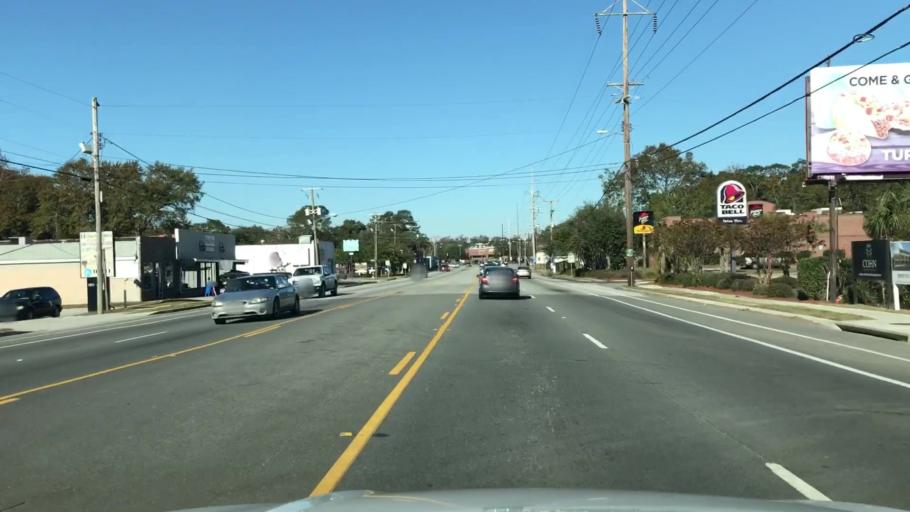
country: US
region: South Carolina
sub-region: Charleston County
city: North Charleston
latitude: 32.7940
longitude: -79.9914
